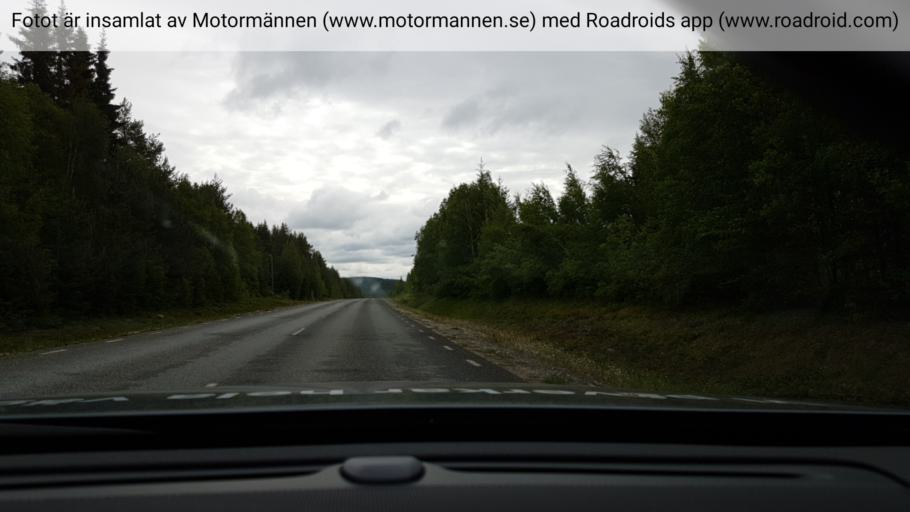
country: SE
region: Vaesterbotten
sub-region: Lycksele Kommun
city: Lycksele
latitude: 64.5658
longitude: 18.5623
